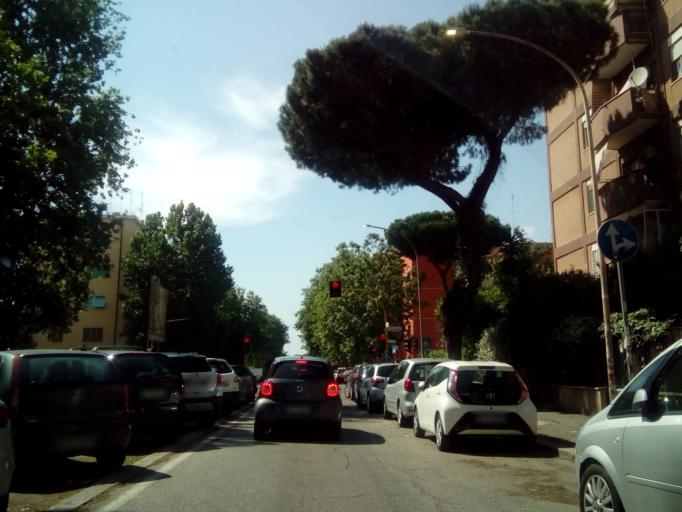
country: IT
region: Latium
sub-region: Citta metropolitana di Roma Capitale
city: Rome
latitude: 41.8577
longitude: 12.5558
